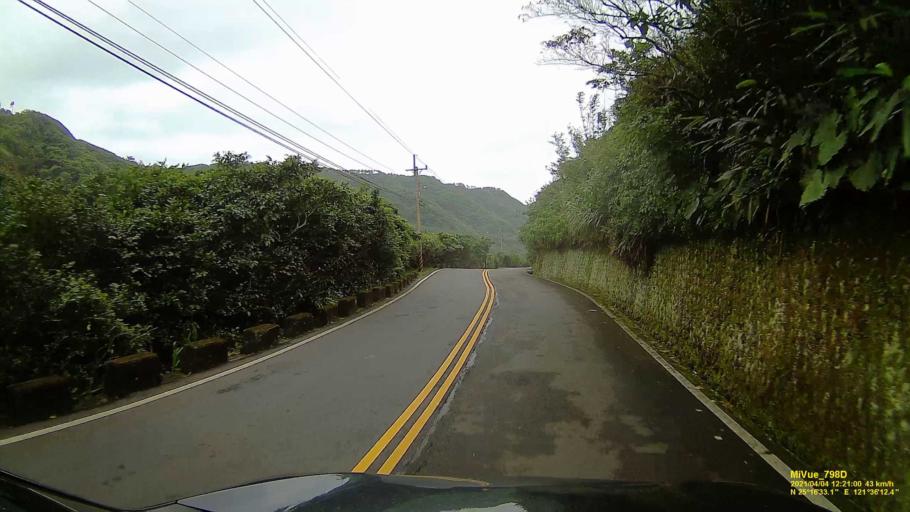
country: TW
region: Taiwan
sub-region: Keelung
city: Keelung
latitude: 25.2762
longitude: 121.6035
